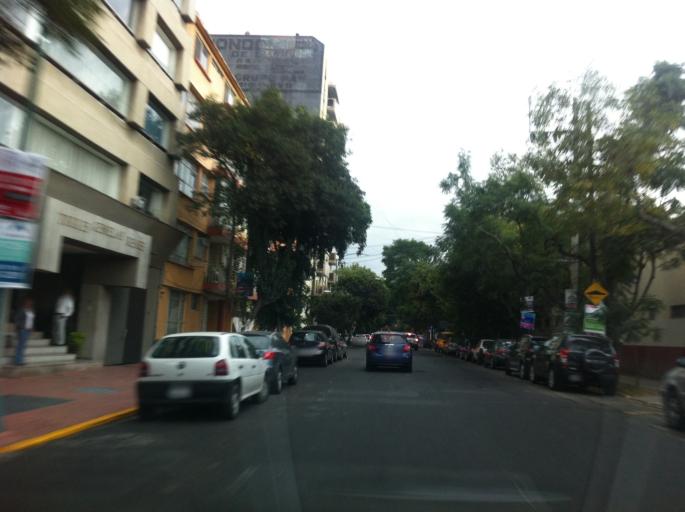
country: MX
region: Mexico City
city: Colonia del Valle
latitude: 19.3850
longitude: -99.1630
